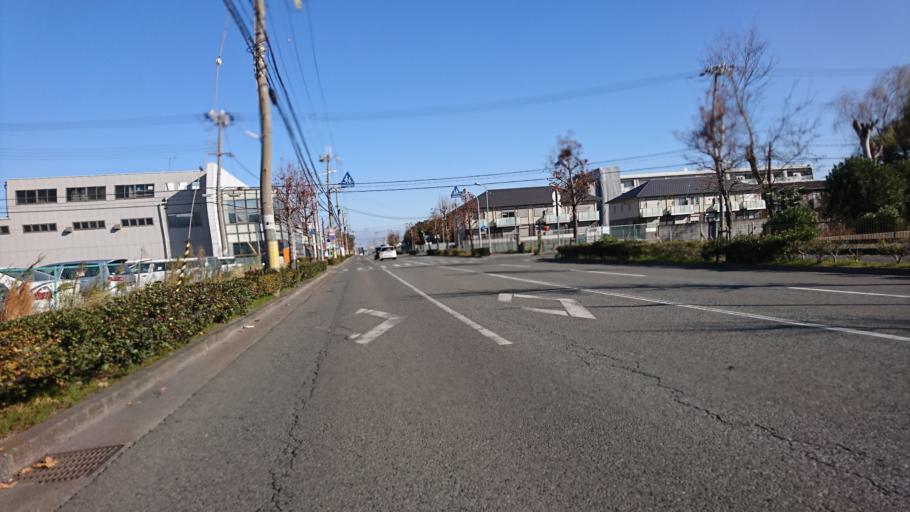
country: JP
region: Hyogo
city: Kakogawacho-honmachi
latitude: 34.7290
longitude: 134.8353
